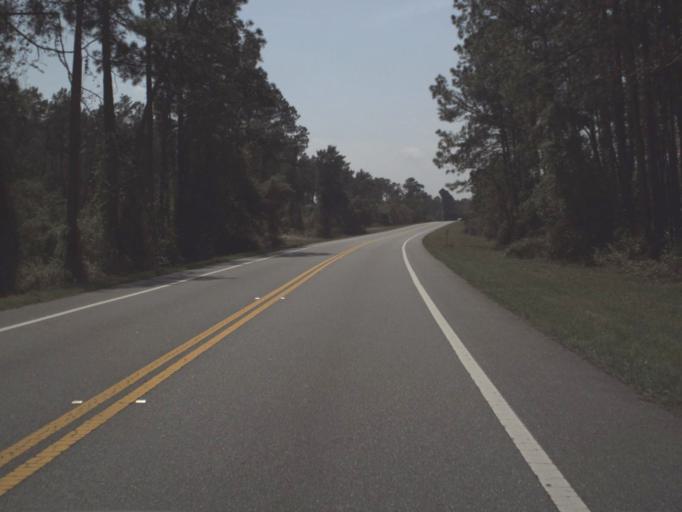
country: US
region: Florida
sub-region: Lake County
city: Astor
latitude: 29.1219
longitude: -81.6185
